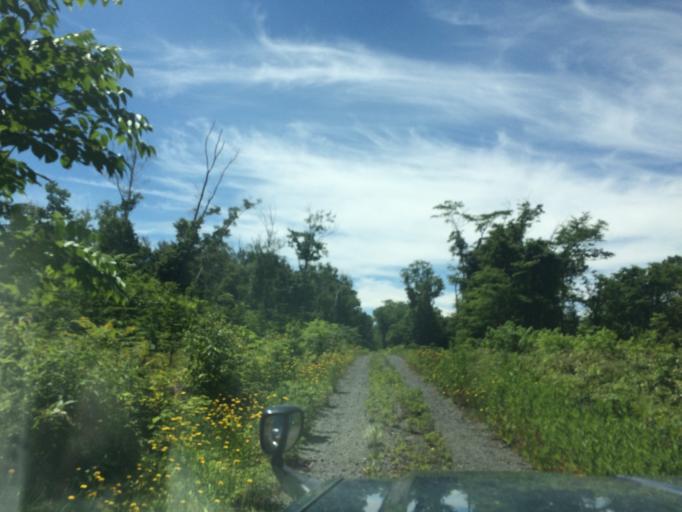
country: JP
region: Hokkaido
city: Niseko Town
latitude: 42.8656
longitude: 140.8158
